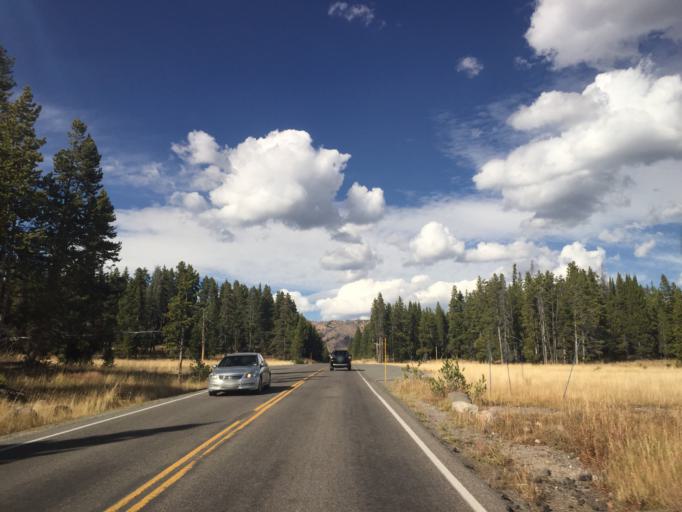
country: US
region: Montana
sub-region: Gallatin County
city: West Yellowstone
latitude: 44.7257
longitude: -110.4939
